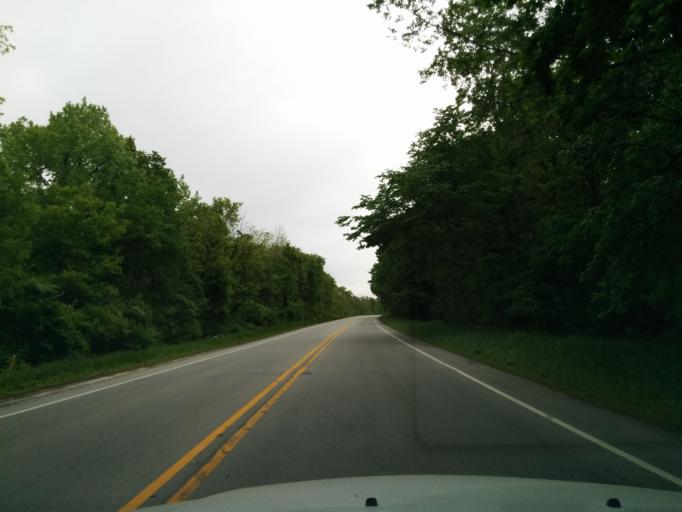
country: US
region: Illinois
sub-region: Cook County
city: Palos Park
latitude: 41.6831
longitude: -87.8403
